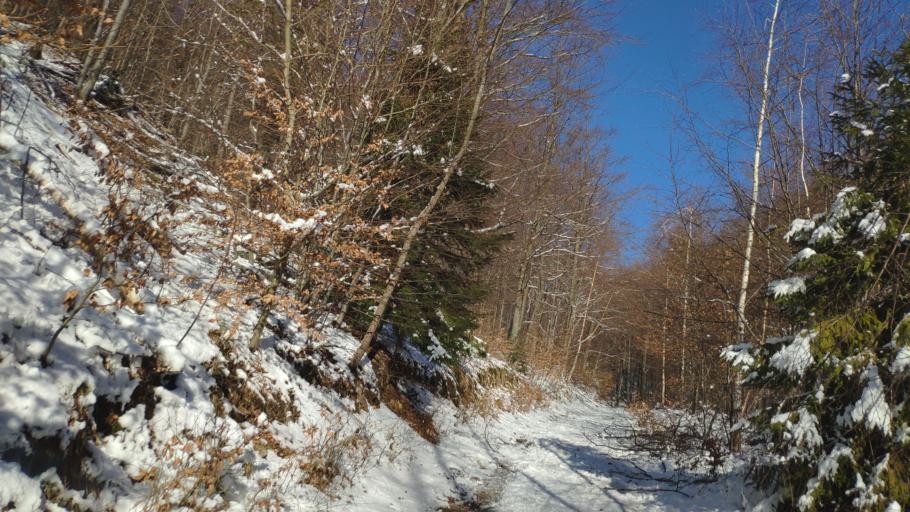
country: SK
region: Kosicky
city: Gelnica
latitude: 48.7611
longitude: 21.0084
